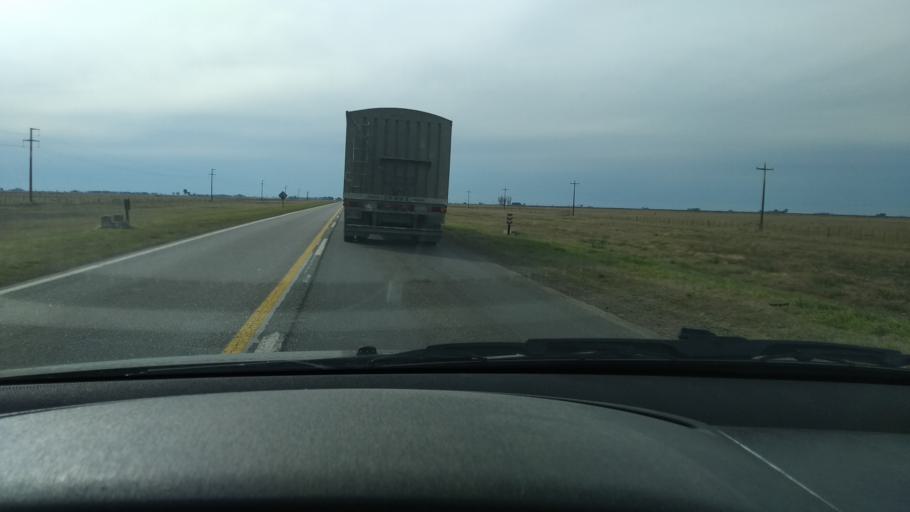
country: AR
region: Buenos Aires
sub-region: Partido de Azul
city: Azul
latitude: -36.7151
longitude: -59.7624
